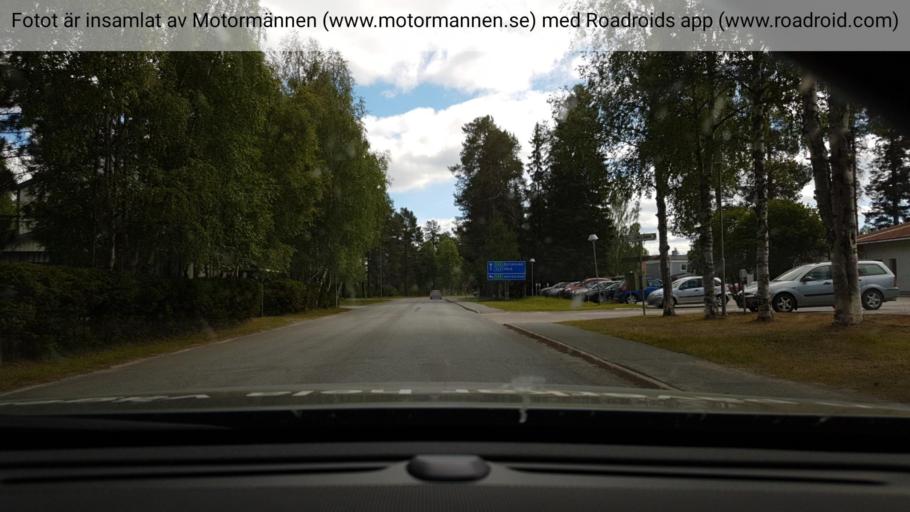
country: SE
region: Vaesterbotten
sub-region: Sorsele Kommun
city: Sorsele
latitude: 65.5384
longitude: 17.5420
